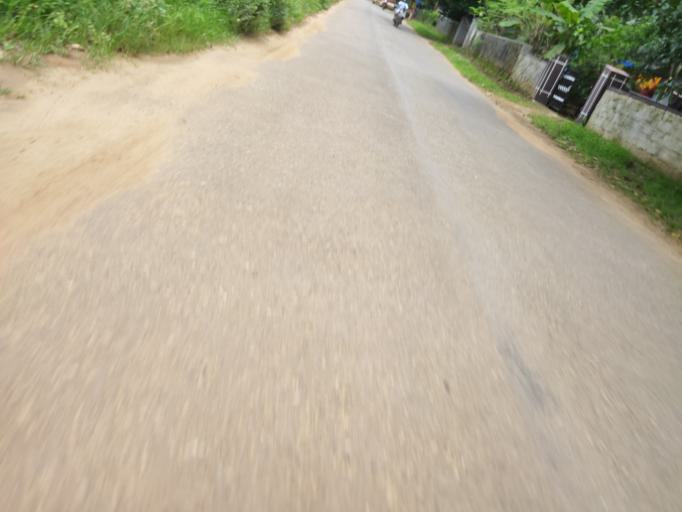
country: IN
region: Kerala
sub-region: Malappuram
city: Manjeri
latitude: 11.2352
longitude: 76.2851
